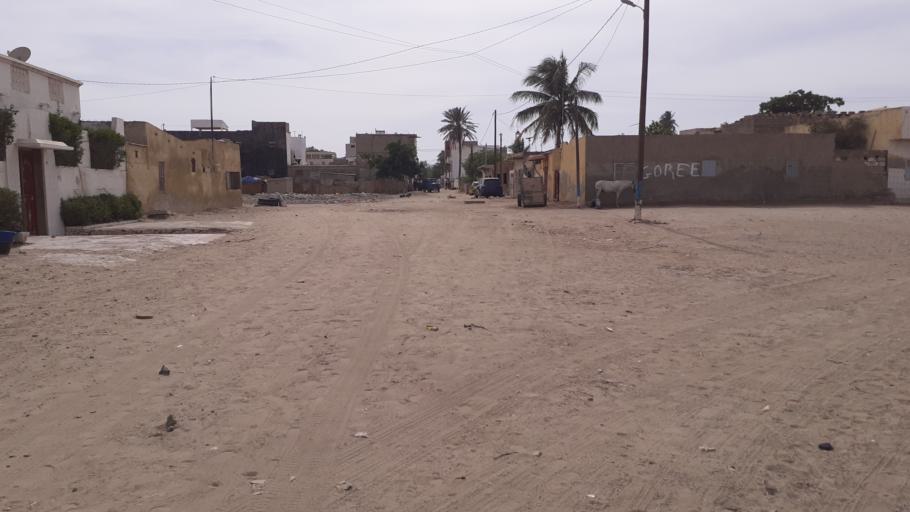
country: SN
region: Saint-Louis
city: Saint-Louis
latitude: 16.0244
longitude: -16.4845
